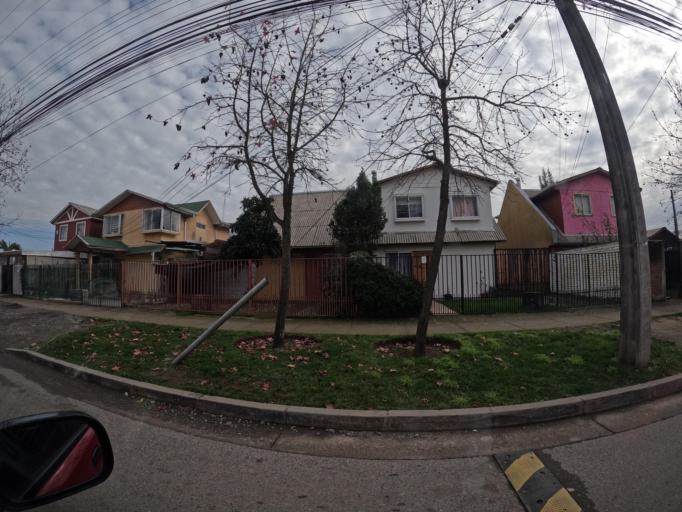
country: CL
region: Maule
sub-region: Provincia de Linares
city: Linares
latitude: -35.8343
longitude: -71.6014
